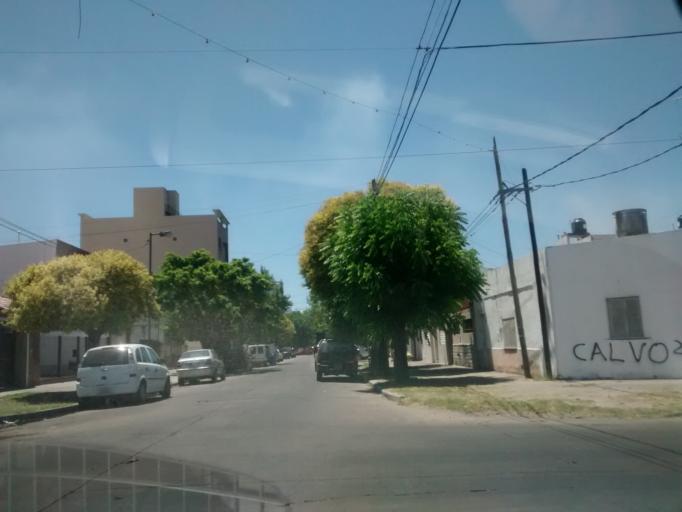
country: AR
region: Buenos Aires
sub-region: Partido de La Plata
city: La Plata
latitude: -34.9475
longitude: -57.9562
